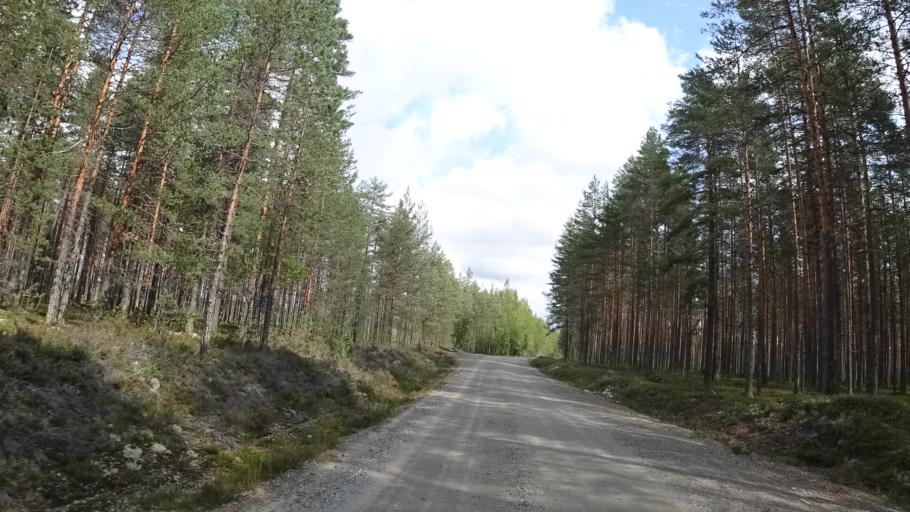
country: FI
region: North Karelia
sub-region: Joensuu
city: Ilomantsi
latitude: 62.9315
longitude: 31.4191
